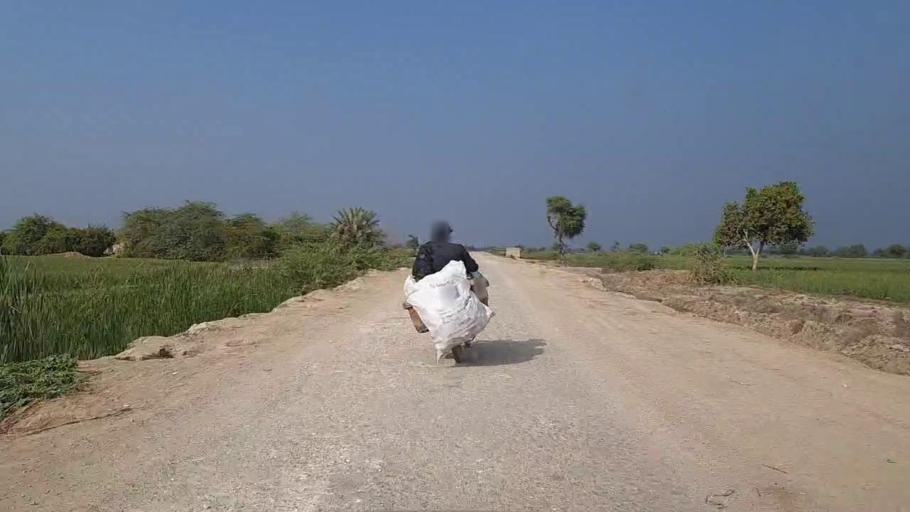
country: PK
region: Sindh
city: Mirwah Gorchani
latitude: 25.4043
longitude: 69.1402
